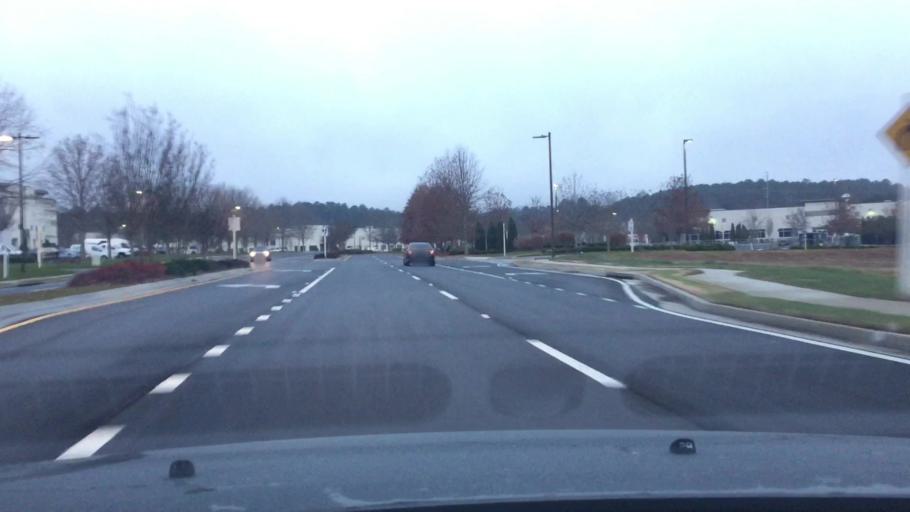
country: US
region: Georgia
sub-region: Cobb County
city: Kennesaw
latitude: 34.0253
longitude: -84.5548
